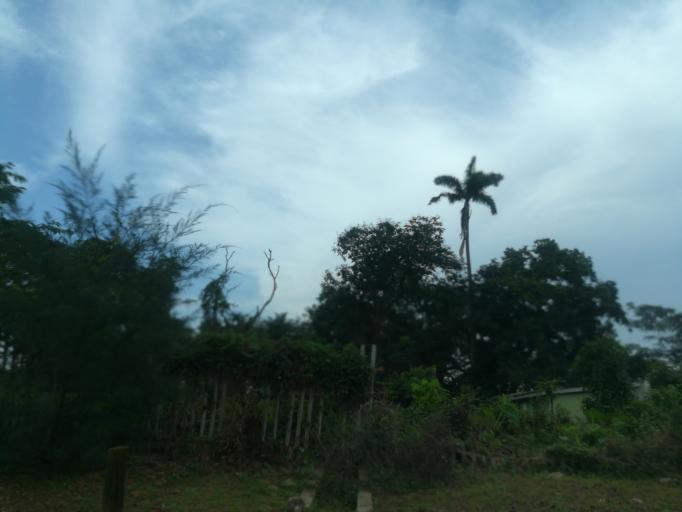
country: NG
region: Oyo
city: Ibadan
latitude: 7.4189
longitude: 3.9043
